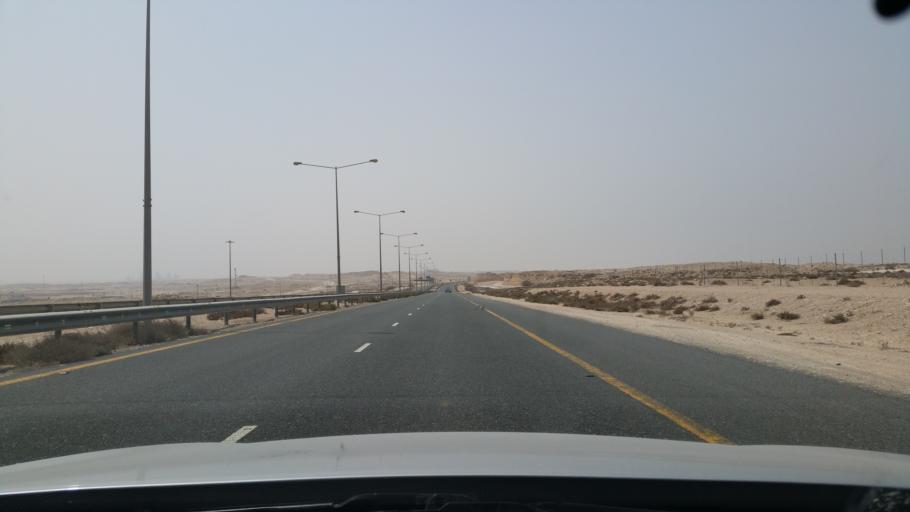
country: QA
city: Umm Bab
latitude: 25.2813
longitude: 50.7913
